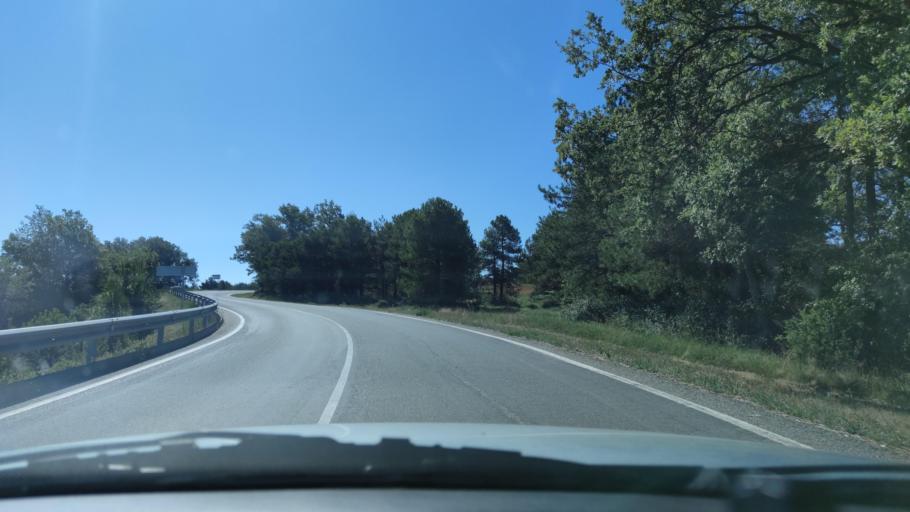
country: ES
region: Catalonia
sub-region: Provincia de Lleida
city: Solsona
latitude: 41.9188
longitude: 1.4997
